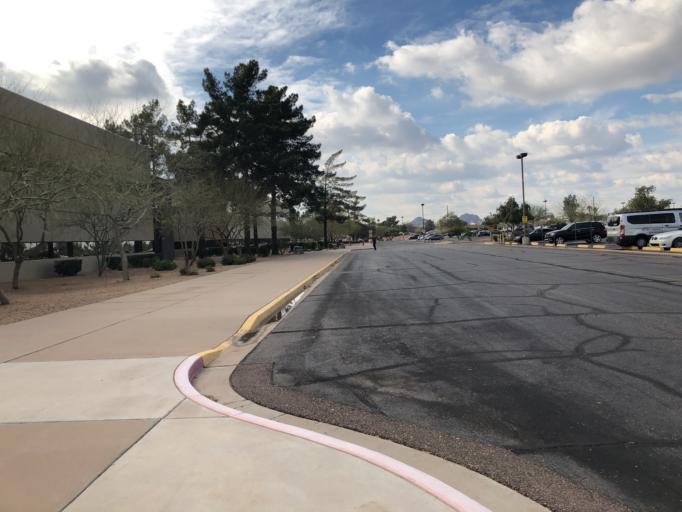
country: US
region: Arizona
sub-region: Maricopa County
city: Tempe
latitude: 33.4608
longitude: -111.9054
